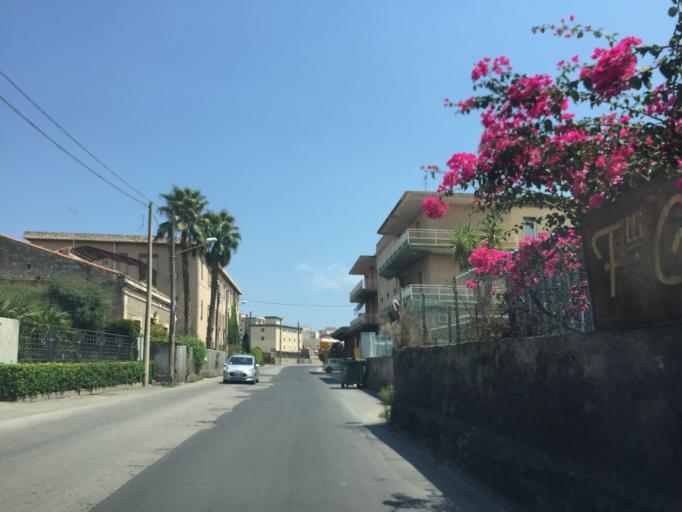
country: IT
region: Sicily
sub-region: Provincia di Siracusa
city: Siracusa
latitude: 37.0693
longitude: 15.2771
